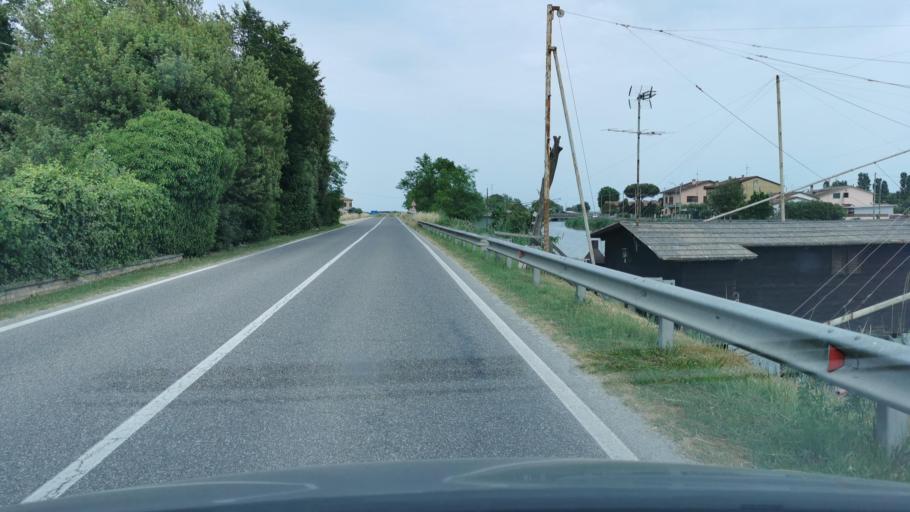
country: IT
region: Emilia-Romagna
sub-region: Provincia di Ravenna
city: Marina Romea
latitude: 44.5627
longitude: 12.2451
